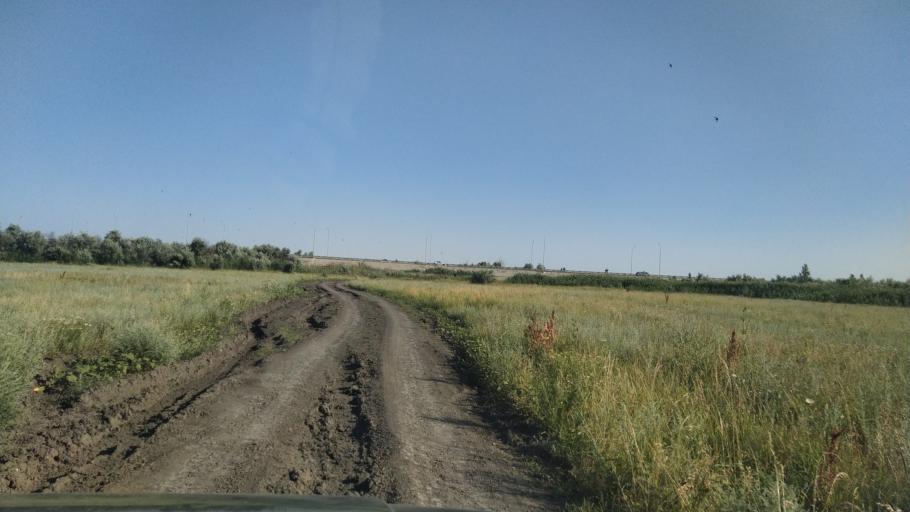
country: RU
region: Rostov
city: Kuleshovka
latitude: 47.1202
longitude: 39.6494
